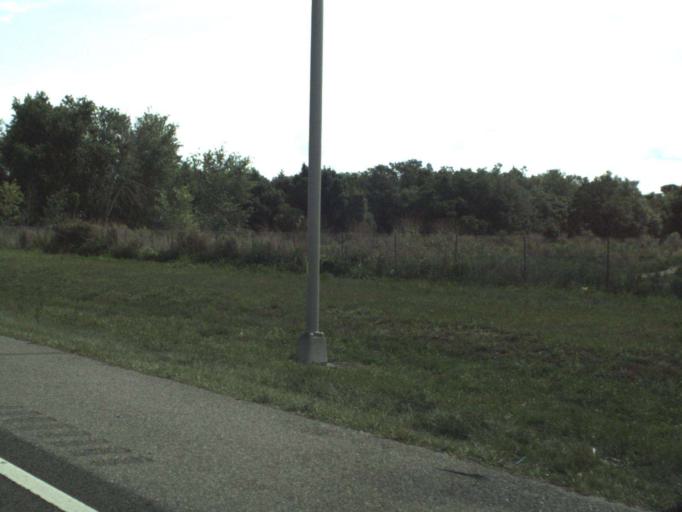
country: US
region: Florida
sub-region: Seminole County
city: Heathrow
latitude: 28.7638
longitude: -81.3604
